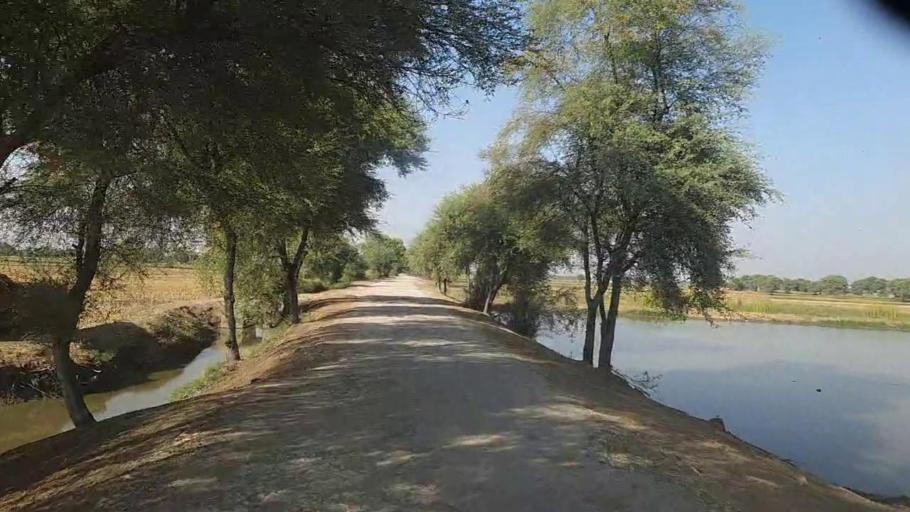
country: PK
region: Sindh
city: Tangwani
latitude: 28.2825
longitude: 68.9844
